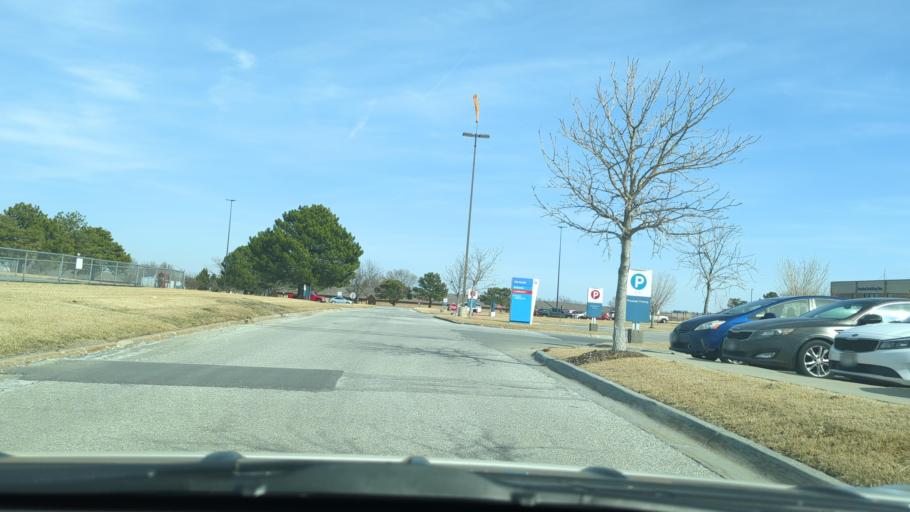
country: US
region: Nebraska
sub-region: Sarpy County
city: Papillion
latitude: 41.1370
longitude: -96.0406
